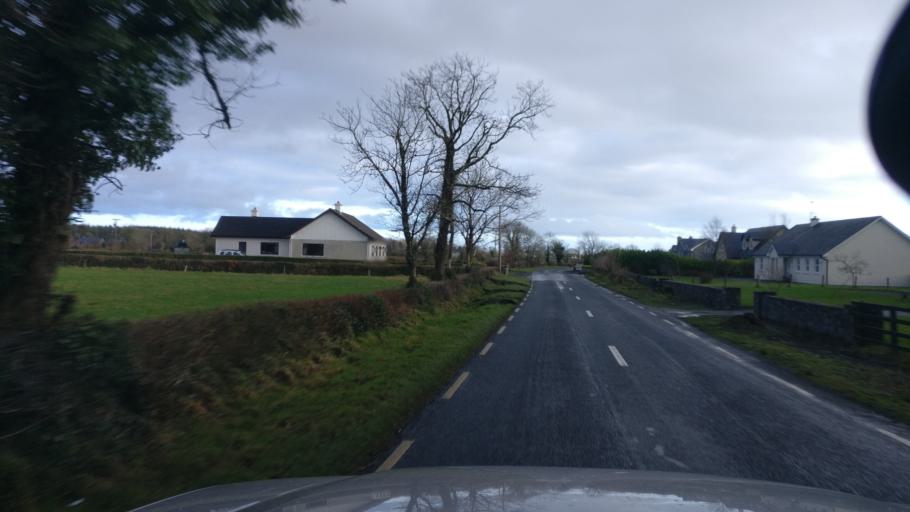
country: IE
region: Connaught
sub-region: County Galway
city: Athenry
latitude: 53.2953
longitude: -8.6521
